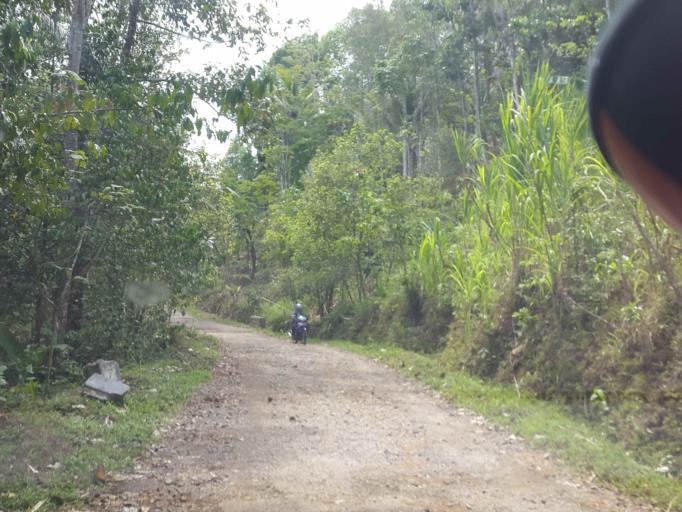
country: ID
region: East Java
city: Krajan
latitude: -8.2333
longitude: 111.1459
